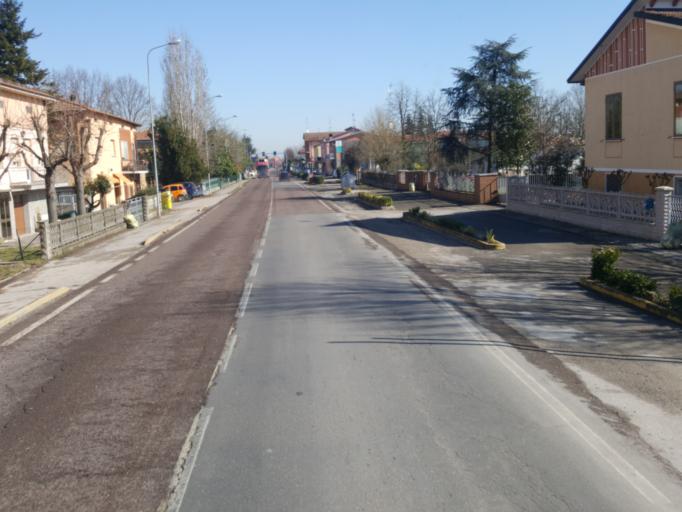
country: IT
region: Emilia-Romagna
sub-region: Provincia di Modena
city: Solara
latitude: 44.7671
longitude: 11.0673
